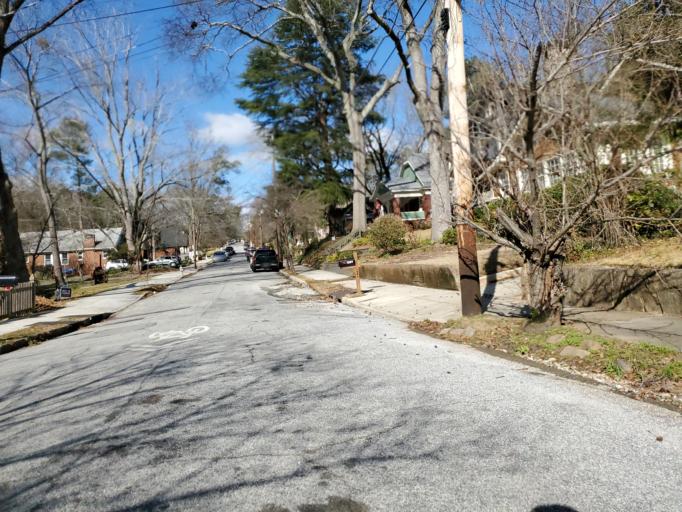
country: US
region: Georgia
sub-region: Fulton County
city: Atlanta
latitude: 33.7271
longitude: -84.3523
